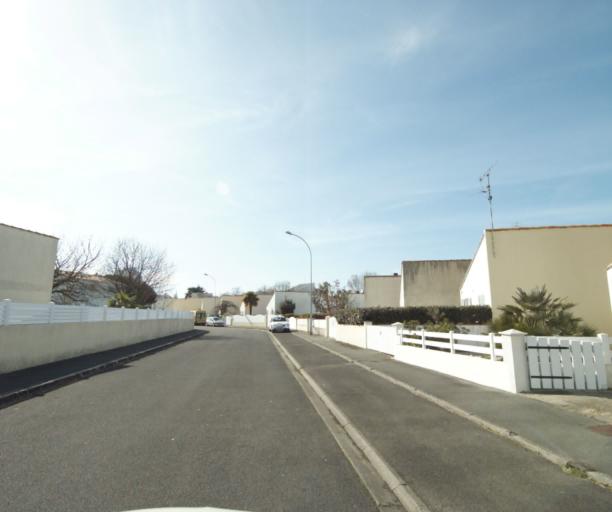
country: FR
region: Poitou-Charentes
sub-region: Departement de la Charente-Maritime
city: La Rochelle
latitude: 46.1713
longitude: -1.1689
